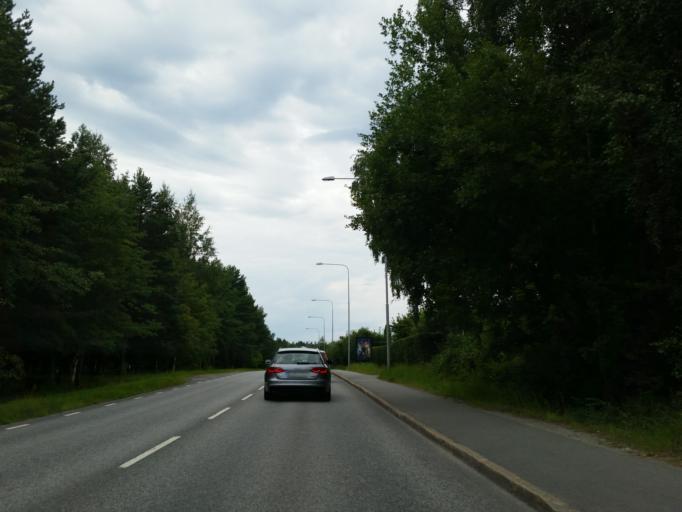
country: SE
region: Stockholm
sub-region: Sodertalje Kommun
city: Soedertaelje
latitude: 59.2018
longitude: 17.6003
